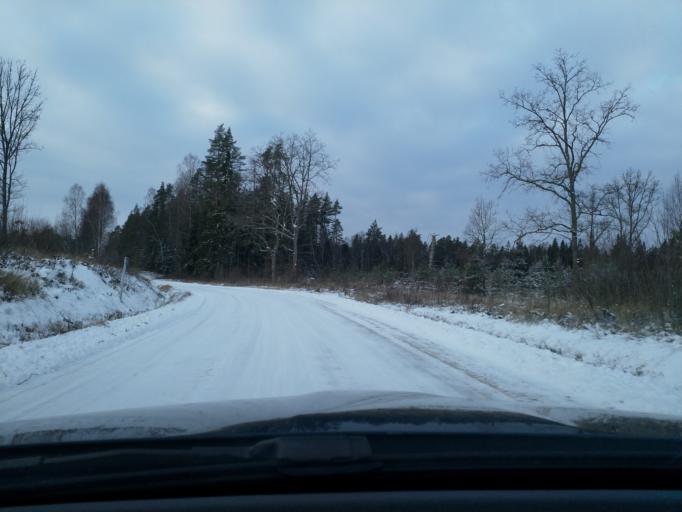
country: LV
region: Kuldigas Rajons
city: Kuldiga
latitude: 56.8680
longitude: 21.8774
